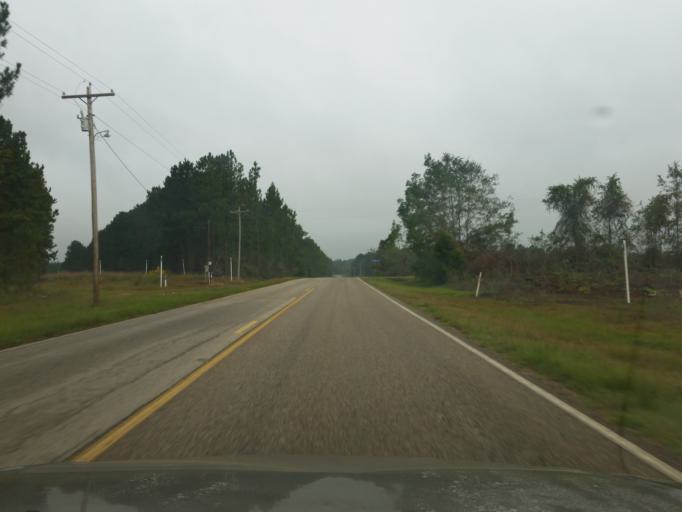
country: US
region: Florida
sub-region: Escambia County
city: Cantonment
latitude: 30.6463
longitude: -87.4477
